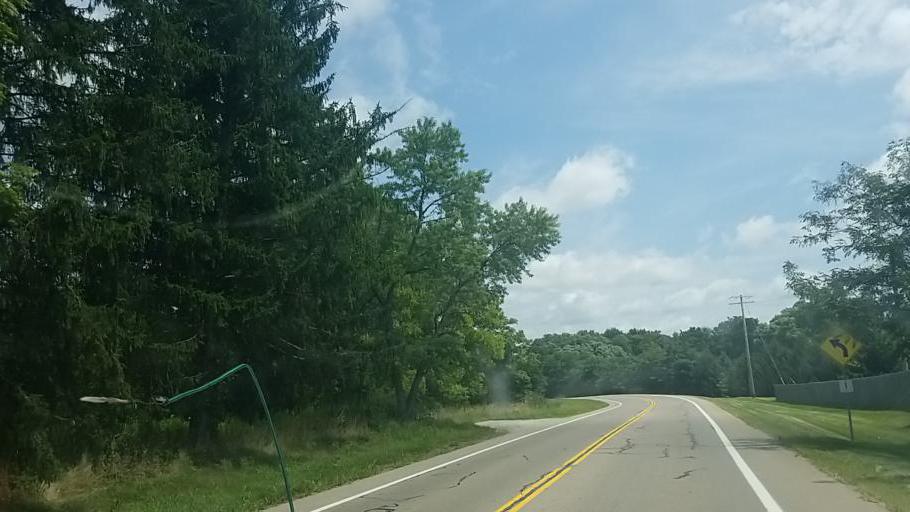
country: US
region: Ohio
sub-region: Fairfield County
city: Pickerington
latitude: 39.9301
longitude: -82.7684
